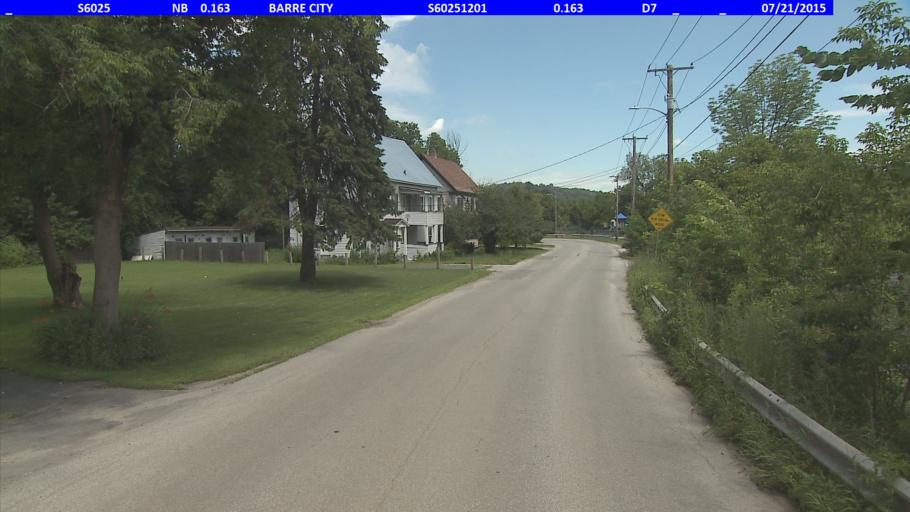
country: US
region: Vermont
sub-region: Washington County
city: Barre
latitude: 44.1995
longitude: -72.5090
